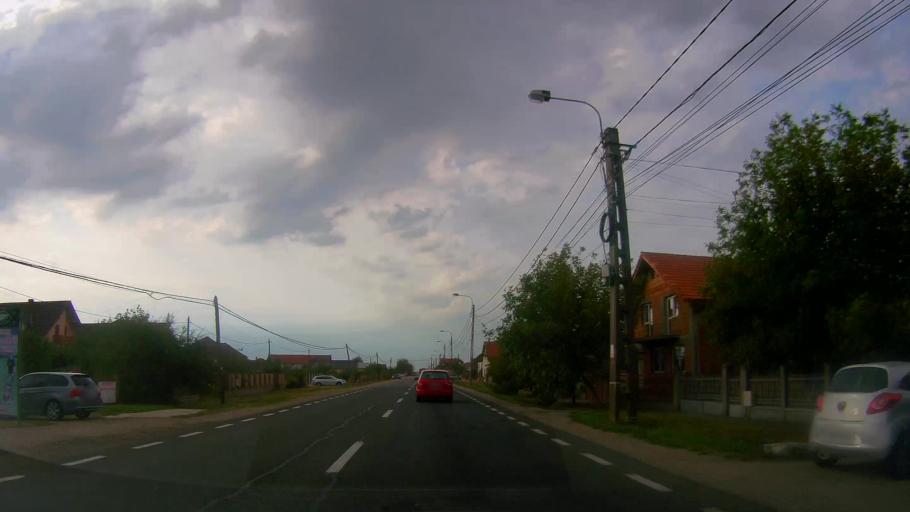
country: RO
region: Satu Mare
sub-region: Oras Ardud
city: Madaras
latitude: 47.7349
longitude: 22.8825
